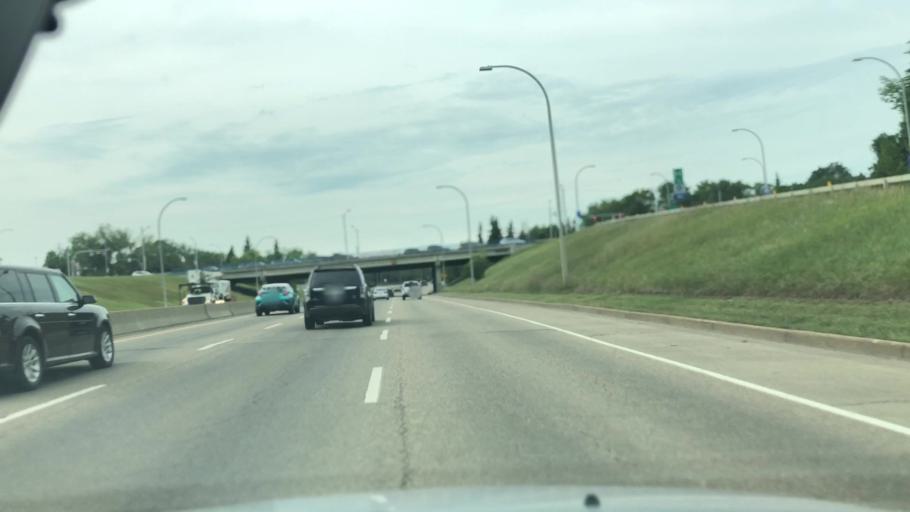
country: CA
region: Alberta
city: Edmonton
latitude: 53.5617
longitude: -113.4447
